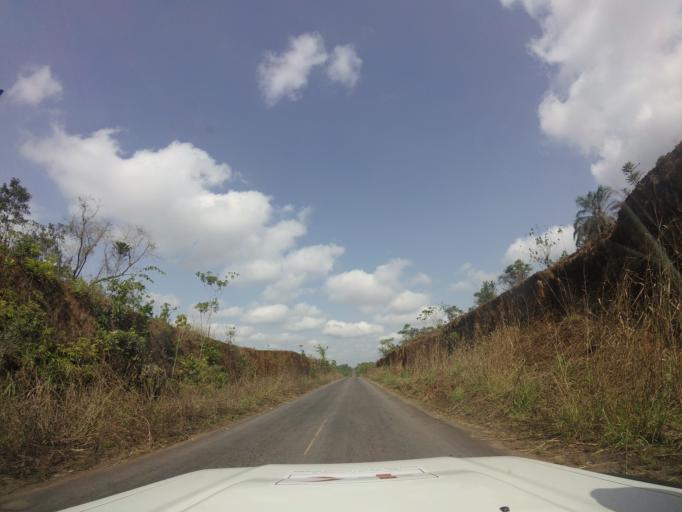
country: LR
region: Bomi
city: Tubmanburg
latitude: 6.6919
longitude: -10.8904
